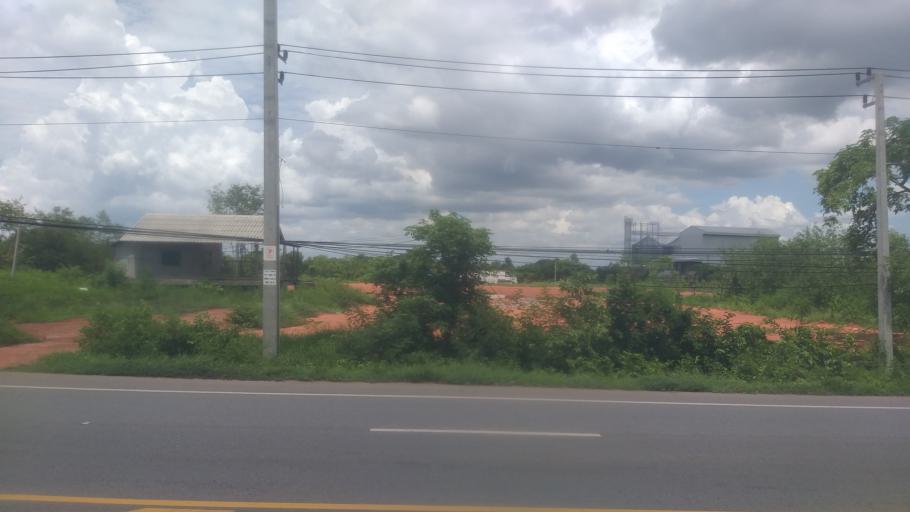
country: TH
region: Nakhon Ratchasima
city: Non Thai
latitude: 15.1103
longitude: 102.1011
